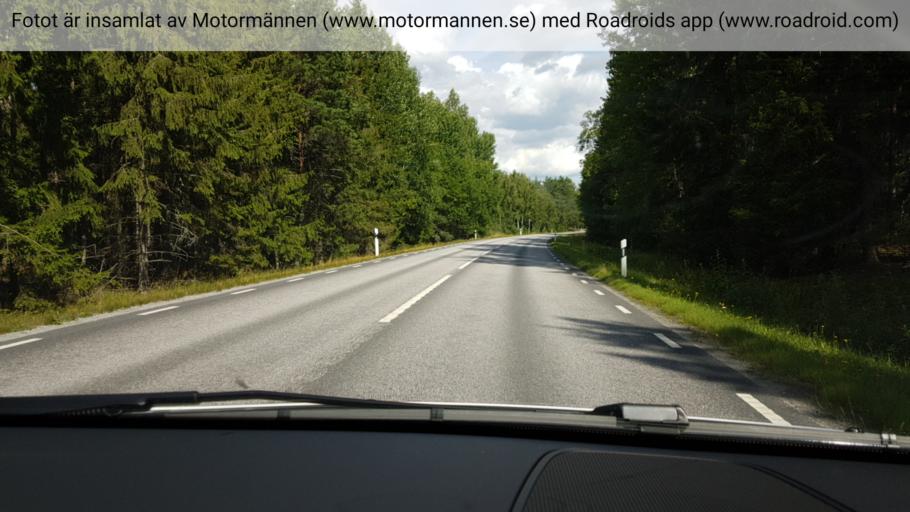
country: SE
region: Stockholm
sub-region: Vallentuna Kommun
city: Vallentuna
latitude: 59.7029
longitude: 18.0437
